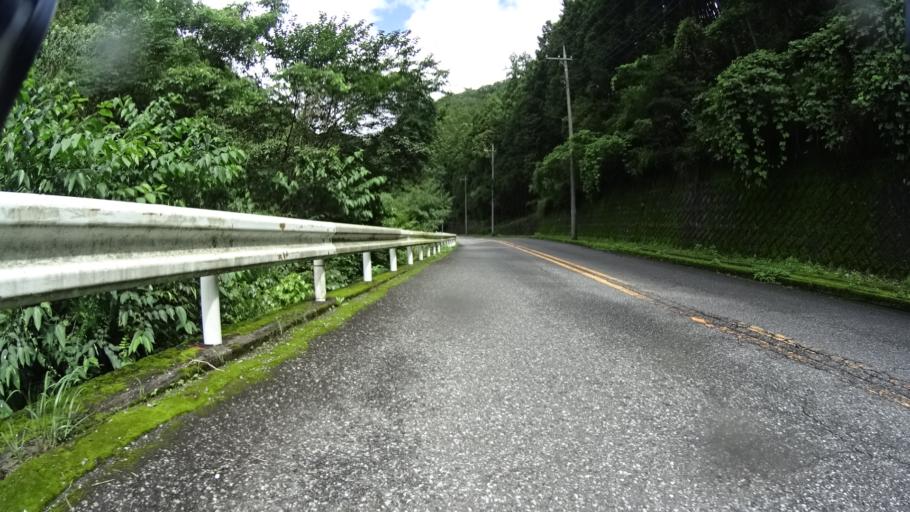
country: JP
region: Tokyo
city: Ome
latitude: 35.8290
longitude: 139.2148
